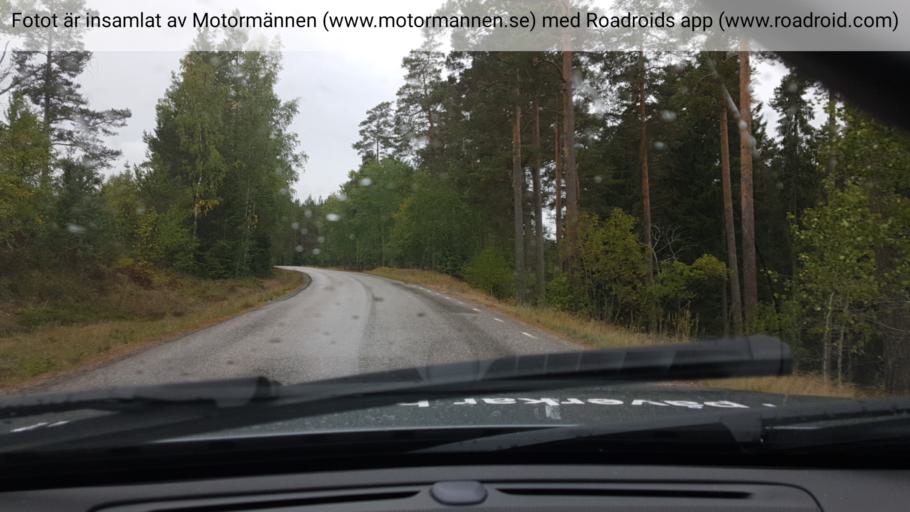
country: SE
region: Stockholm
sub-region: Nynashamns Kommun
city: Osmo
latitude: 59.0685
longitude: 17.8760
